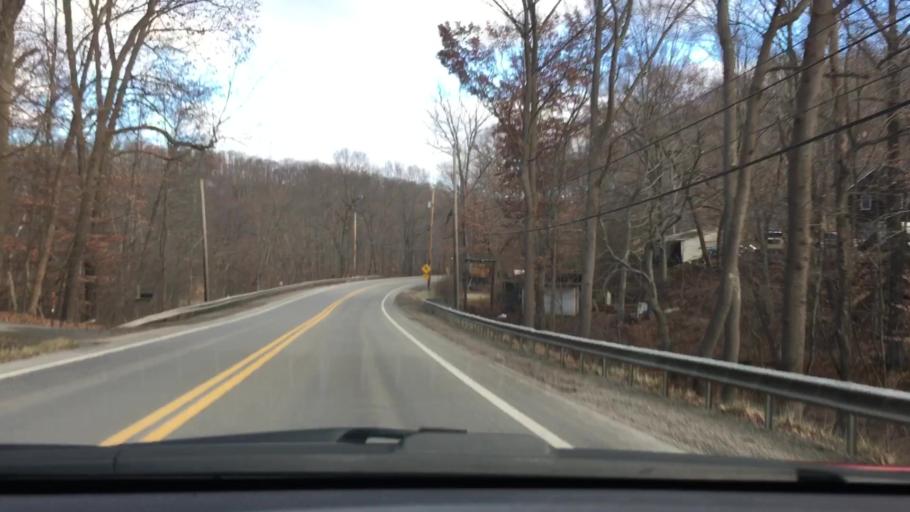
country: US
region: Pennsylvania
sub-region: Westmoreland County
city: Avonmore
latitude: 40.6246
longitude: -79.4291
